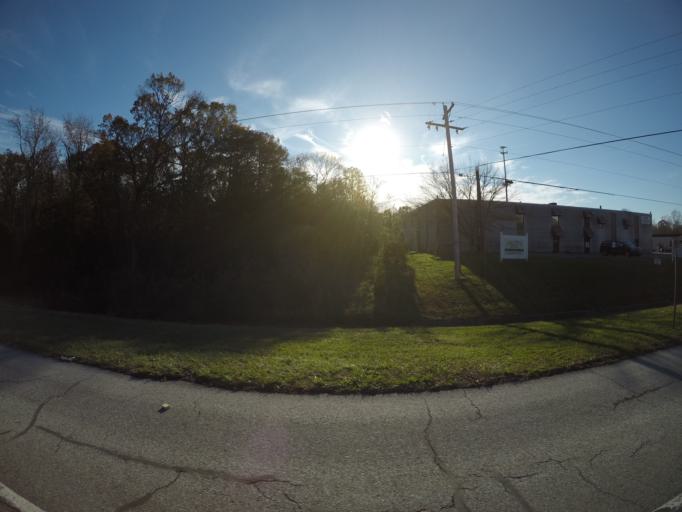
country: US
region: Maryland
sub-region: Saint Mary's County
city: Leonardtown
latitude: 38.3211
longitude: -76.6728
